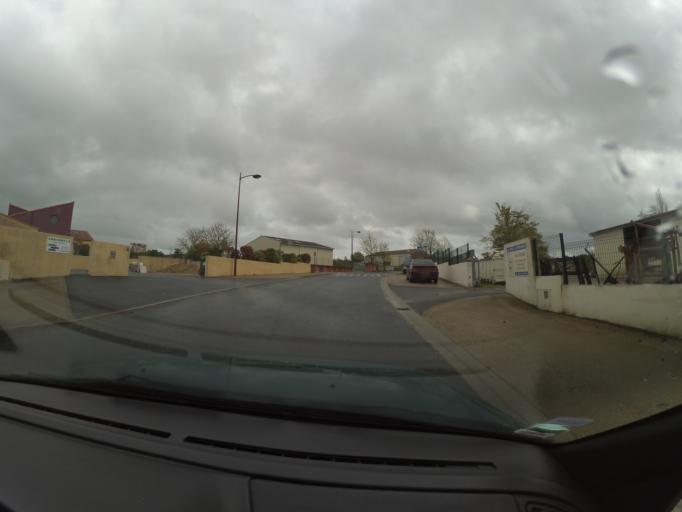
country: FR
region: Pays de la Loire
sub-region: Departement de la Loire-Atlantique
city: Monnieres
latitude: 47.1348
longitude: -1.3514
